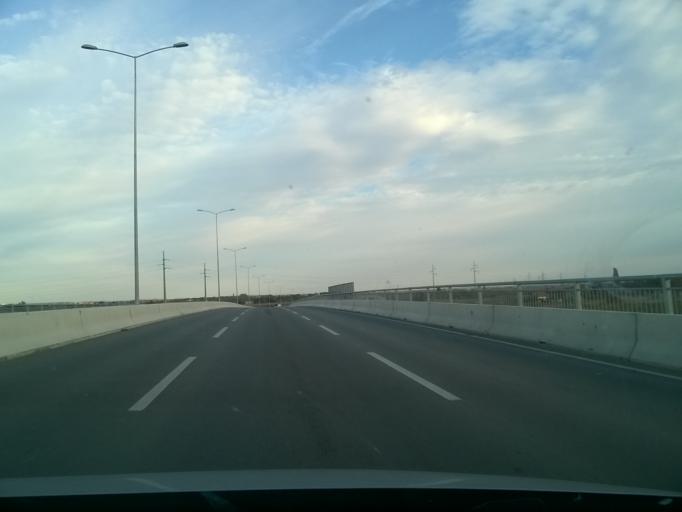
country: RS
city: Ovca
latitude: 44.8568
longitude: 20.5150
